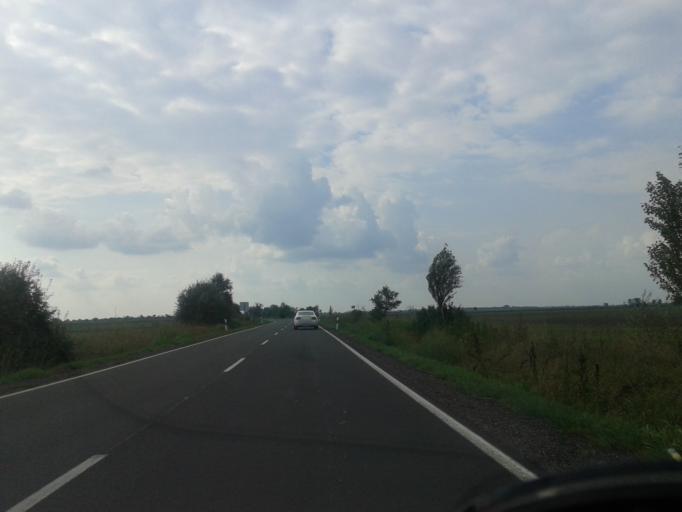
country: HU
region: Bacs-Kiskun
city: Akaszto
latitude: 46.7471
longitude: 19.1292
